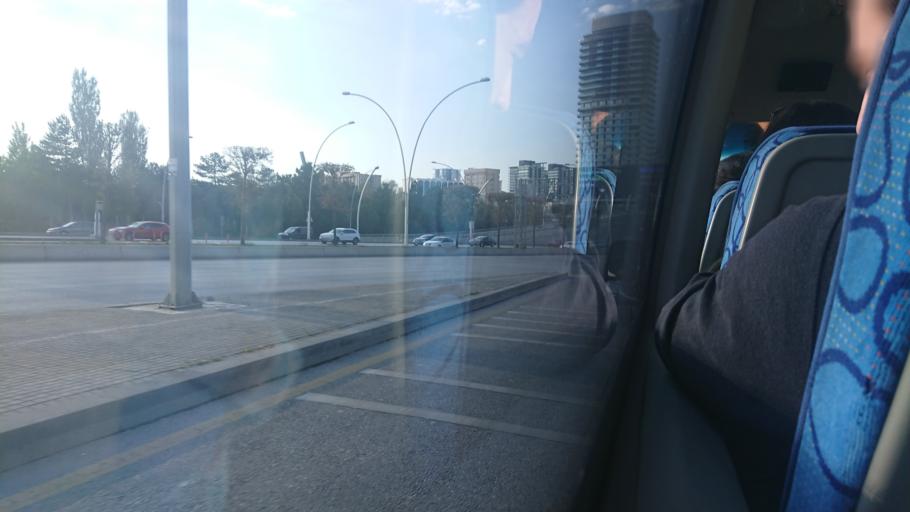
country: TR
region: Ankara
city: Ankara
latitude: 39.9060
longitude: 32.7872
